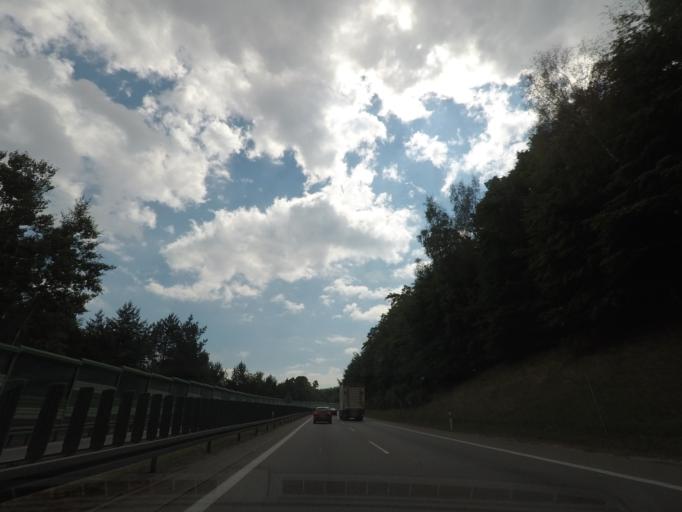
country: PL
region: Pomeranian Voivodeship
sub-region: Gdynia
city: Pogorze
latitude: 54.5280
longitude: 18.4562
